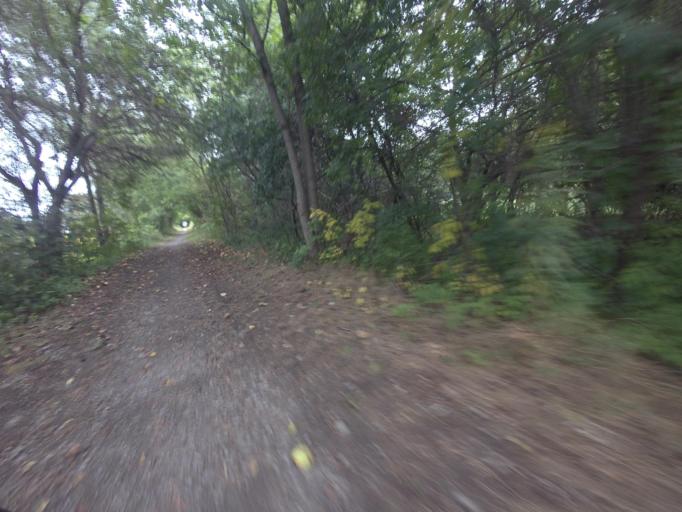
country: CA
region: Ontario
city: Omemee
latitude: 44.3420
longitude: -78.7449
